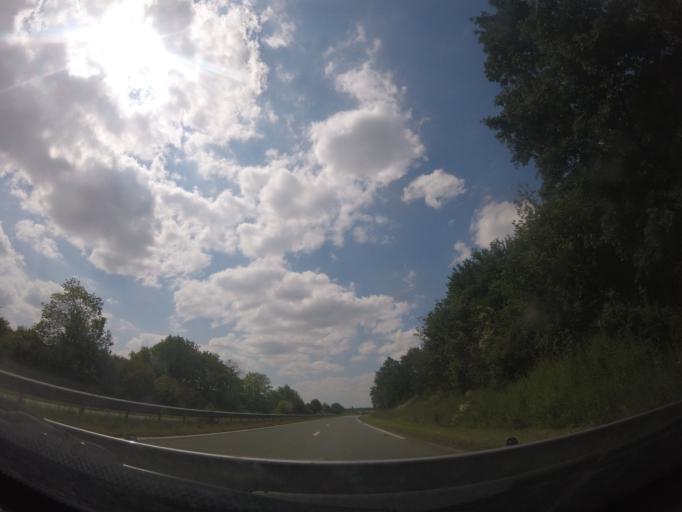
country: FR
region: Poitou-Charentes
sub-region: Departement de la Charente-Maritime
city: Saint-Porchaire
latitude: 45.8141
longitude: -0.7832
